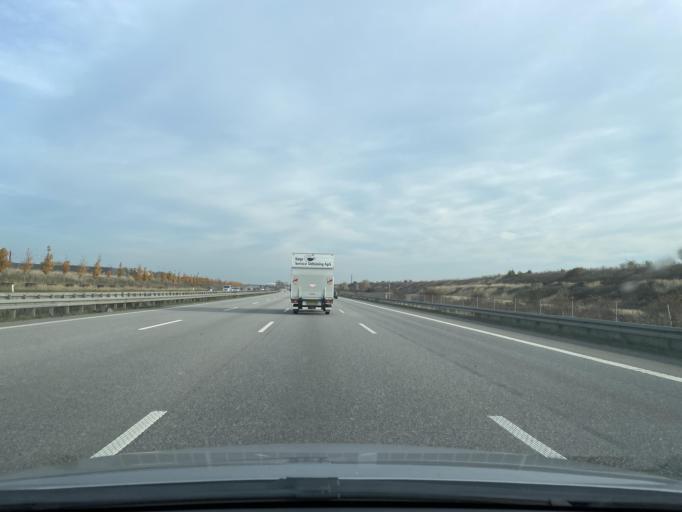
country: DK
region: Zealand
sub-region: Greve Kommune
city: Greve
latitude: 55.5744
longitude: 12.2522
